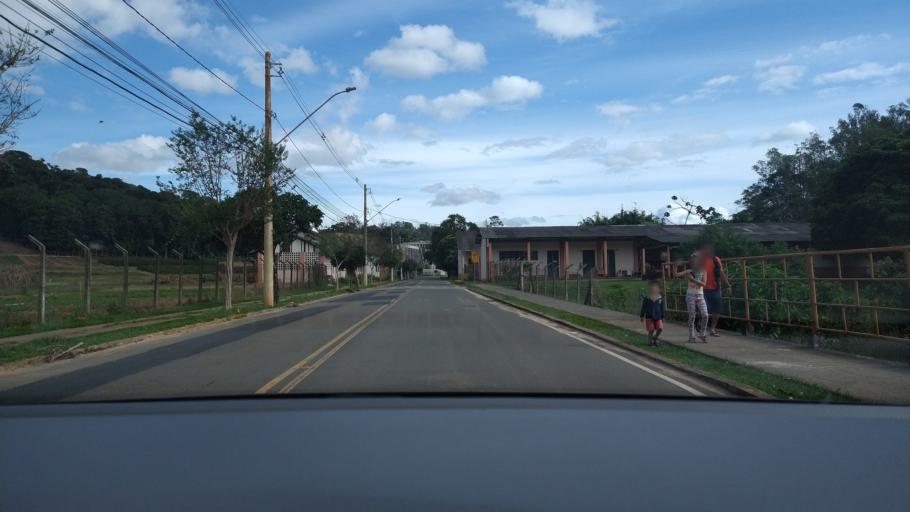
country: BR
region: Minas Gerais
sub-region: Vicosa
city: Vicosa
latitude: -20.7669
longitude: -42.8701
